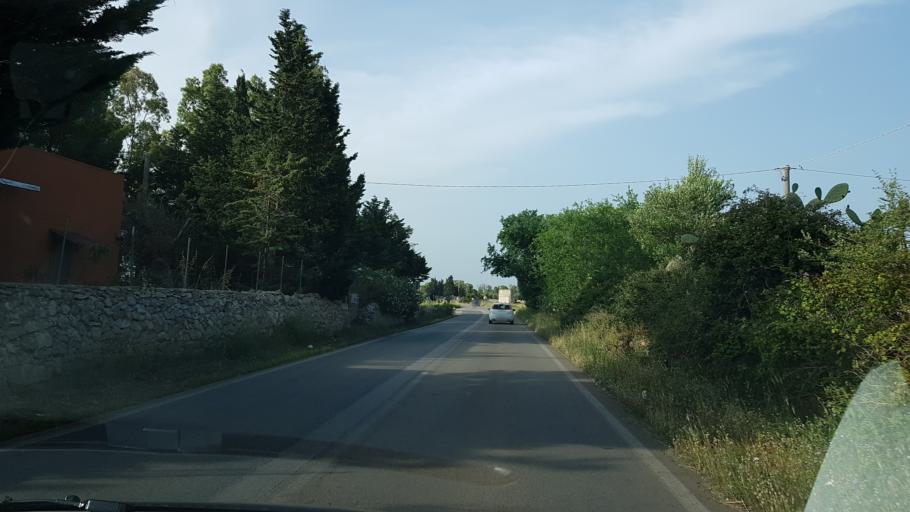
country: IT
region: Apulia
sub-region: Provincia di Lecce
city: Porto Cesareo
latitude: 40.3065
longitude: 17.8622
